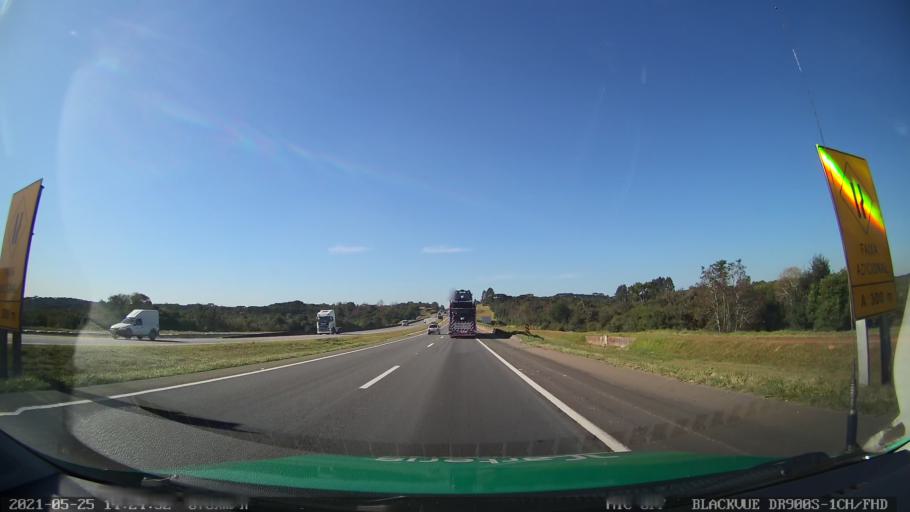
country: BR
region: Parana
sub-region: Piraquara
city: Piraquara
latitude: -25.4826
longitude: -49.1060
